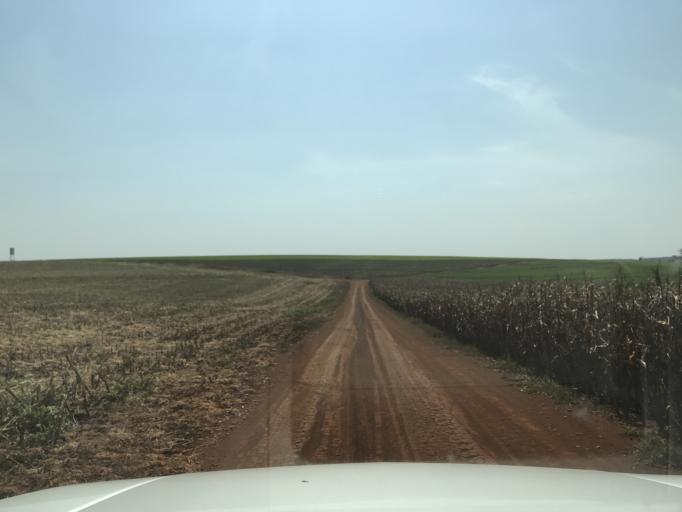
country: BR
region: Parana
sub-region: Palotina
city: Palotina
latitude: -24.2317
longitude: -53.7454
